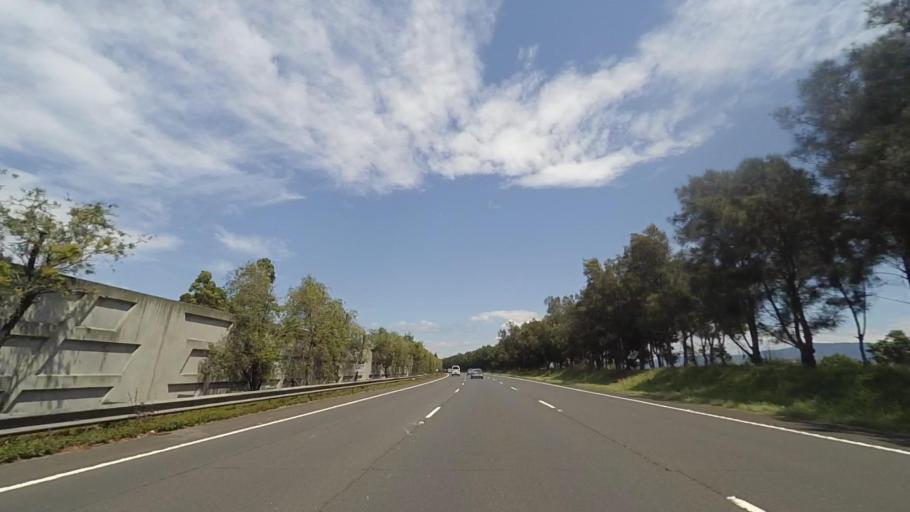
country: AU
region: New South Wales
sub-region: Wollongong
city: Berkeley
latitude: -34.4661
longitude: 150.8435
